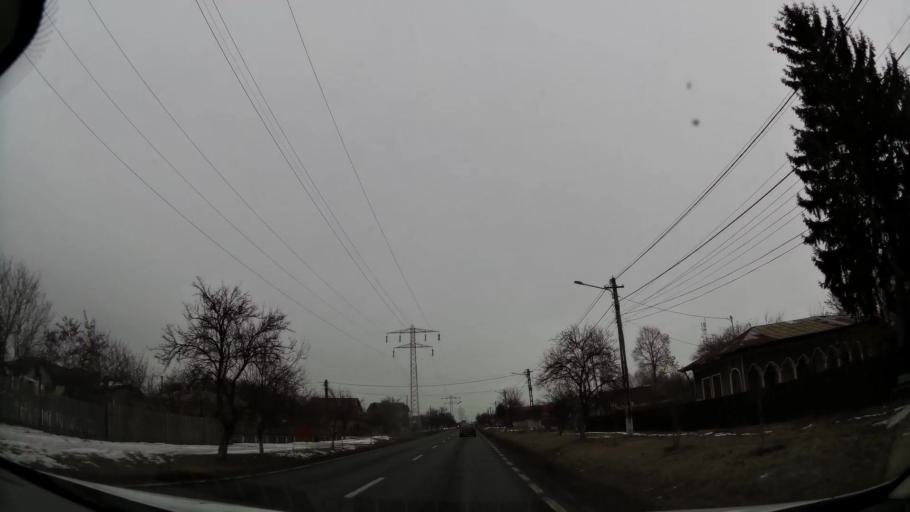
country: RO
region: Dambovita
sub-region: Comuna Salcioara
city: Salcioara
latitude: 44.7379
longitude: 25.6045
